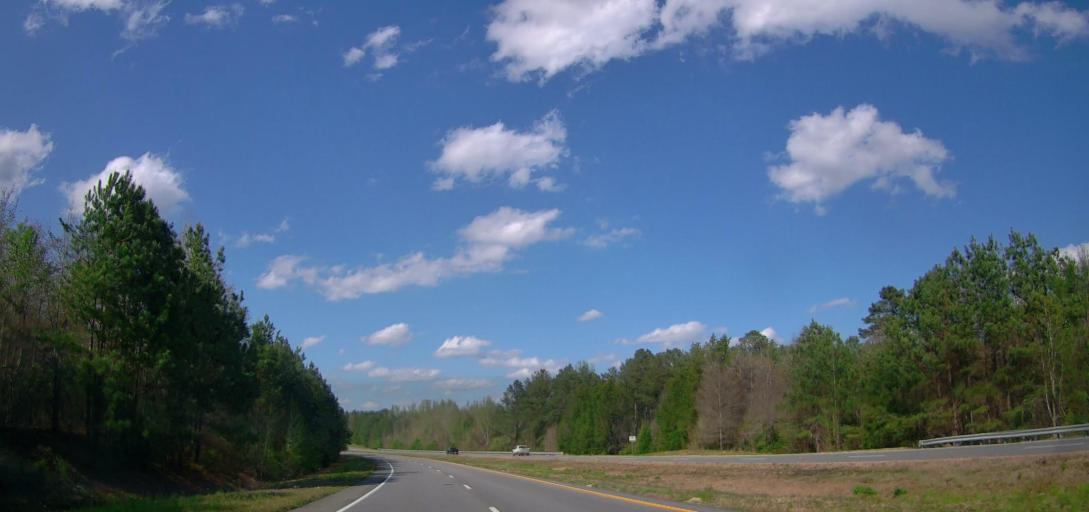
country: US
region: Georgia
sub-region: Baldwin County
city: Hardwick
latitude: 32.9839
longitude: -83.2125
